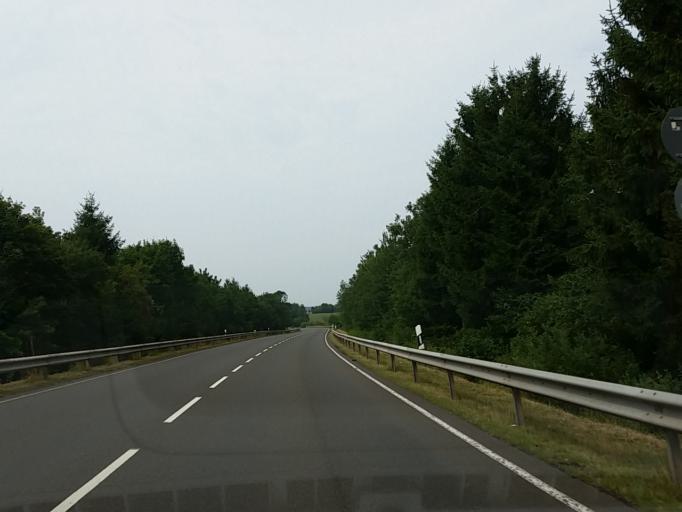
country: DE
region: Rheinland-Pfalz
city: Hinzert-Polert
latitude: 49.6752
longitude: 6.9095
